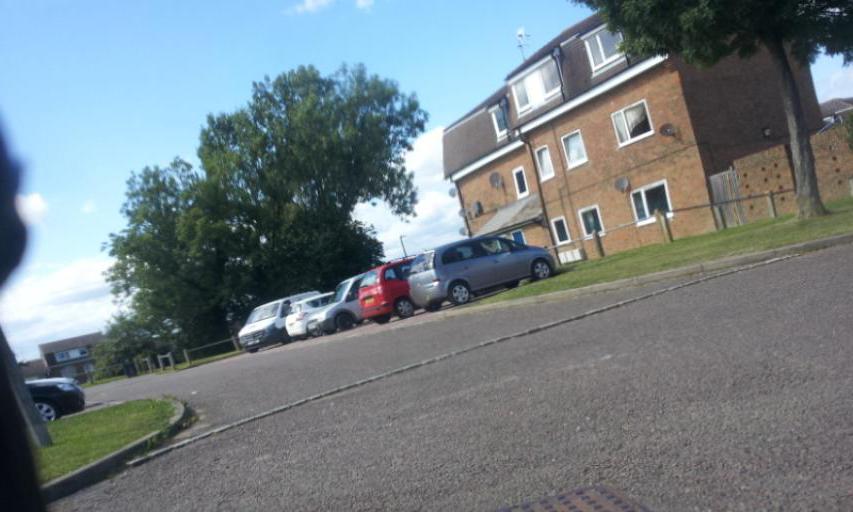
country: GB
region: England
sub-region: Kent
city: Marden
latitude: 51.1716
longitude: 0.4917
